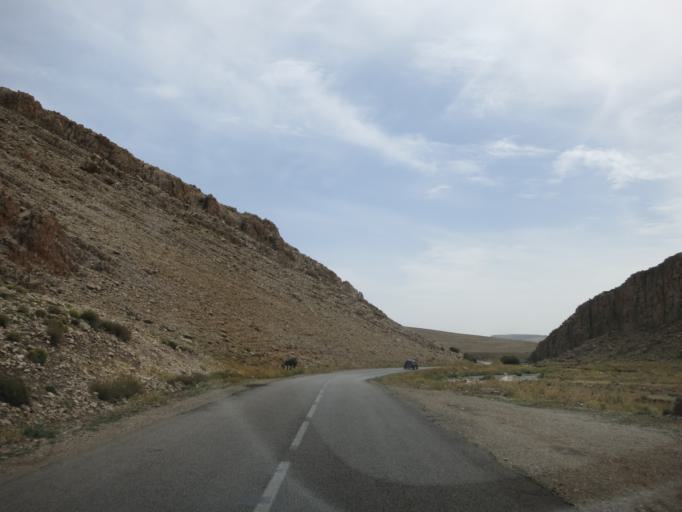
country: MA
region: Meknes-Tafilalet
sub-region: Khenifra
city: Itzer
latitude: 33.1521
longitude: -5.0637
